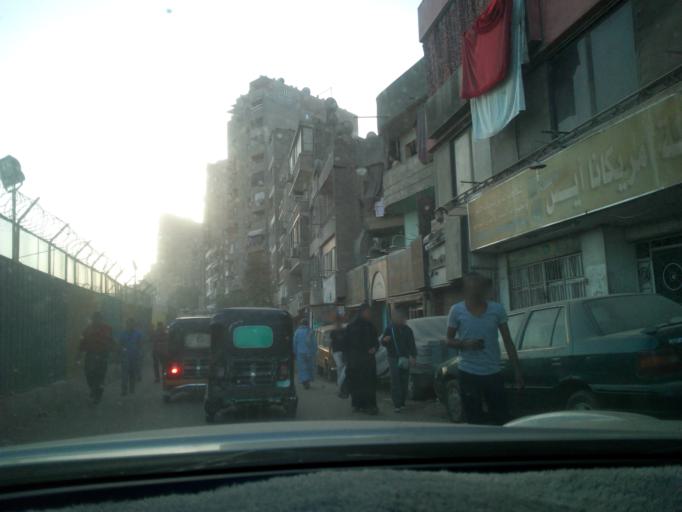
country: EG
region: Muhafazat al Qalyubiyah
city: Al Khankah
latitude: 30.1265
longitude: 31.3506
